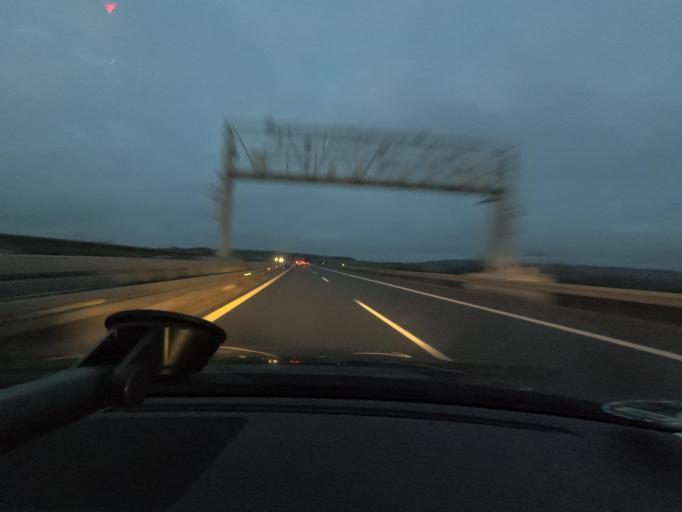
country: DE
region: Bavaria
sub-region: Upper Franconia
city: Lautertal
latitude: 50.3045
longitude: 10.9630
